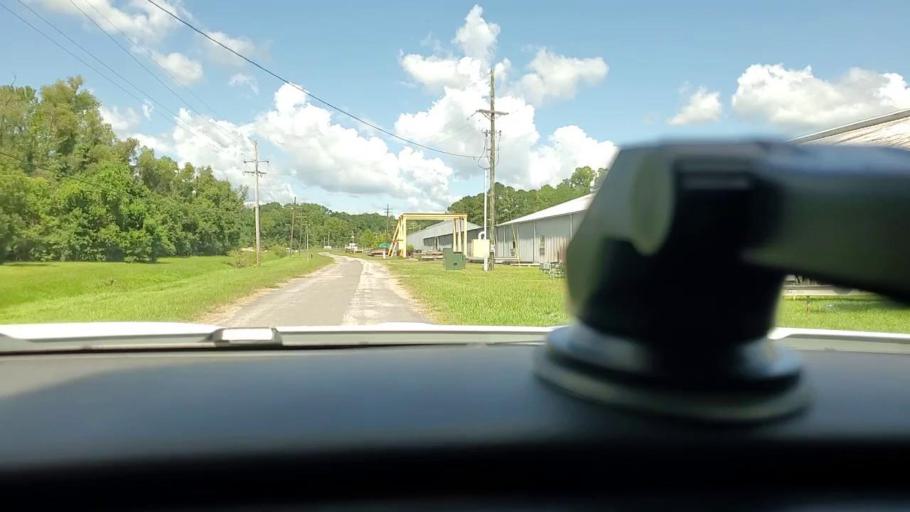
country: US
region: Mississippi
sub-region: Warren County
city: Beechwood
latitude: 32.3068
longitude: -90.8630
